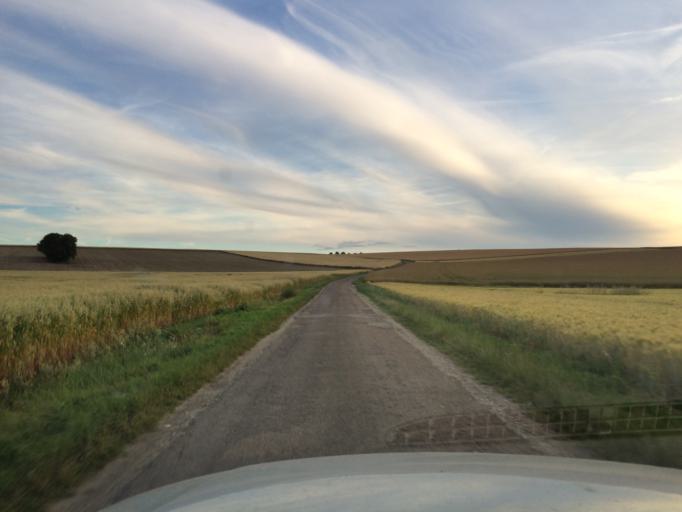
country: FR
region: Bourgogne
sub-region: Departement de l'Yonne
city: Aillant-sur-Tholon
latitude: 47.8604
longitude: 3.3832
